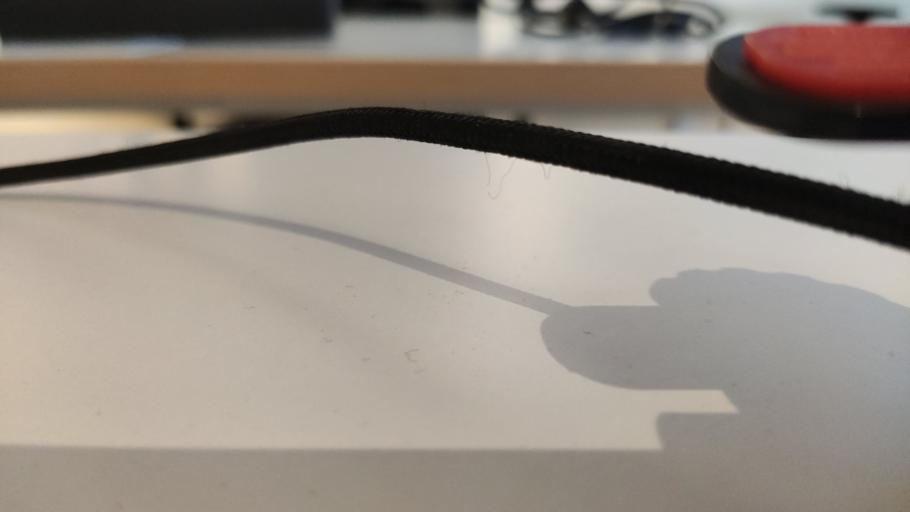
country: RU
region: Moskovskaya
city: Ruza
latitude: 55.8121
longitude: 36.2962
